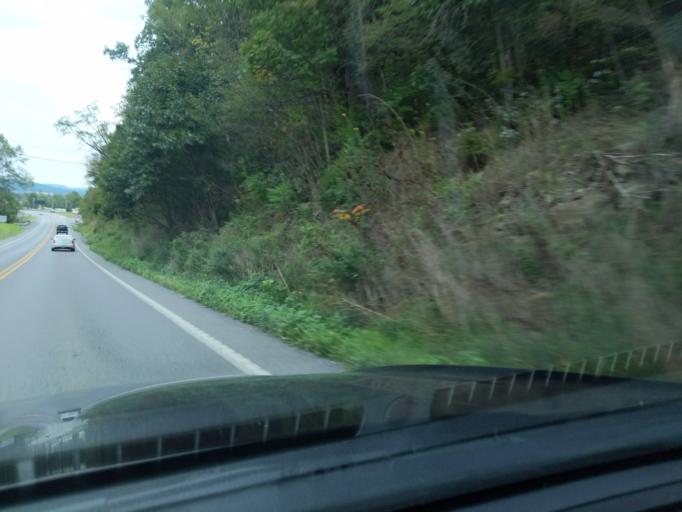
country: US
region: Pennsylvania
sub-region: Blair County
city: Duncansville
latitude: 40.4155
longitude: -78.4378
